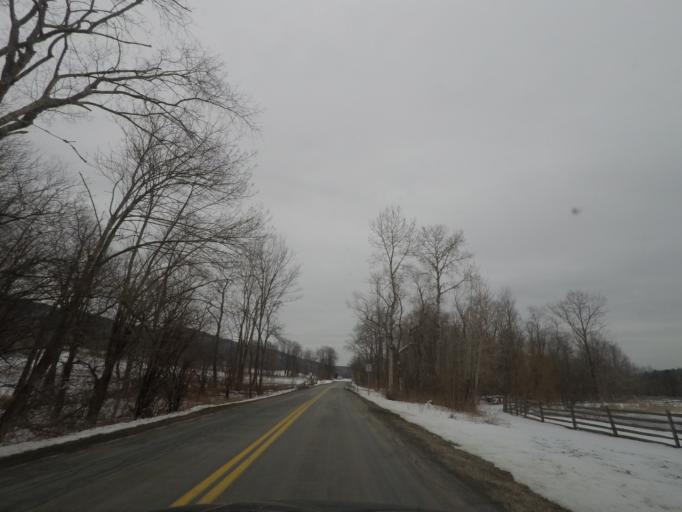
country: US
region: Massachusetts
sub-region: Berkshire County
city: Lanesborough
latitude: 42.5975
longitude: -73.3579
